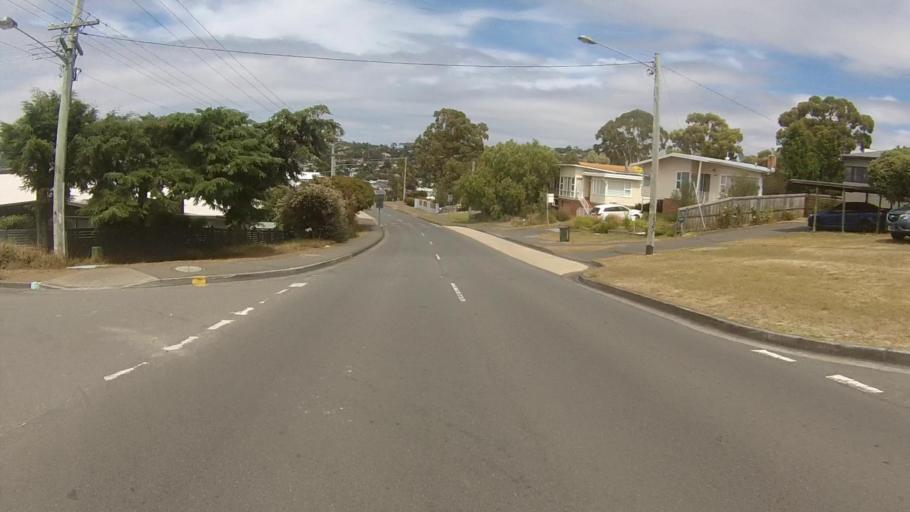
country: AU
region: Tasmania
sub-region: Kingborough
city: Blackmans Bay
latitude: -42.9957
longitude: 147.3236
